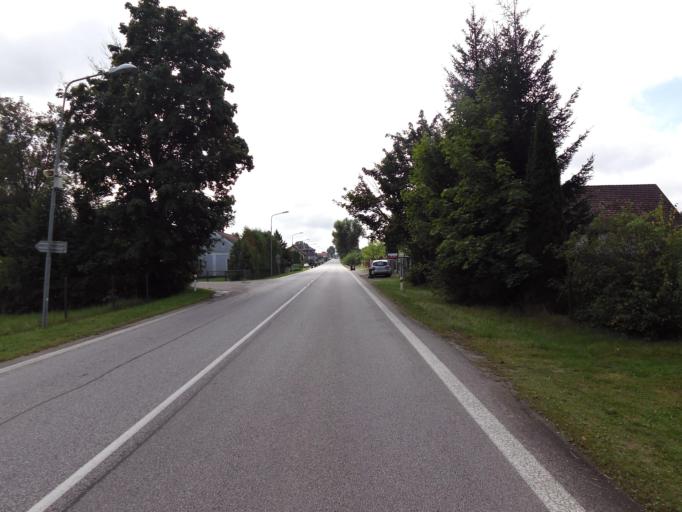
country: CZ
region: Jihocesky
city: Suchdol nad Luznici
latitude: 48.9032
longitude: 14.8810
